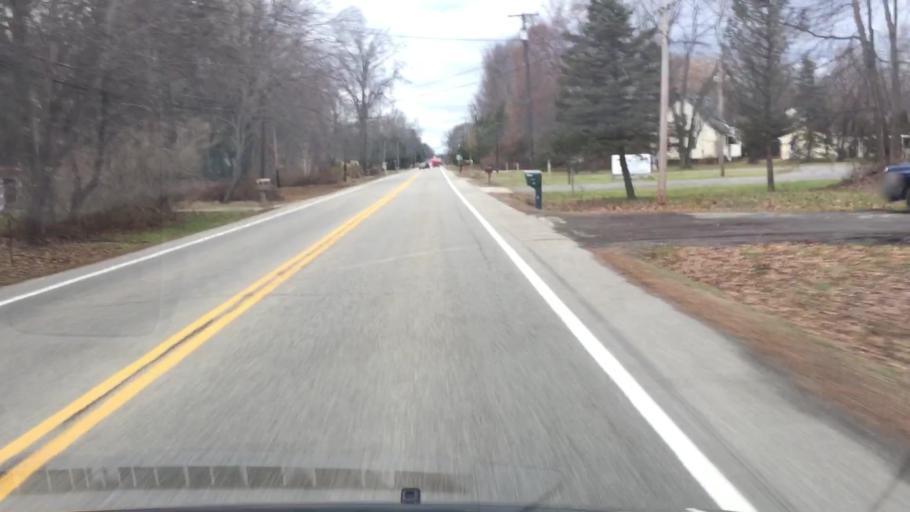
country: US
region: Ohio
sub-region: Summit County
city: Macedonia
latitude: 41.2983
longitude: -81.5261
